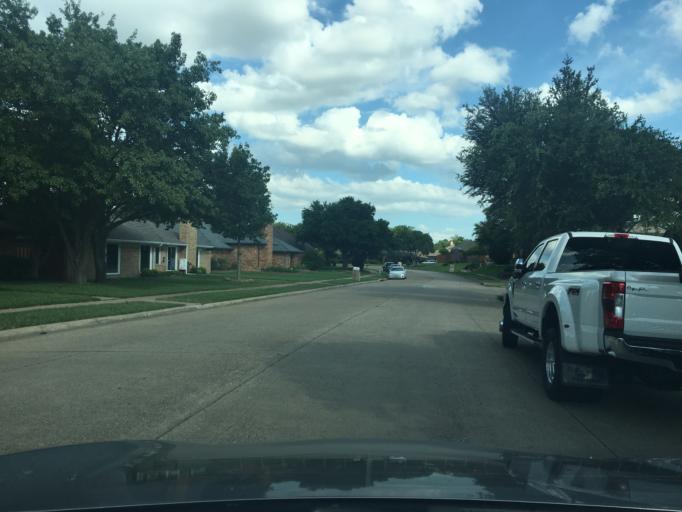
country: US
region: Texas
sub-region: Dallas County
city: Richardson
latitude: 32.9410
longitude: -96.6812
